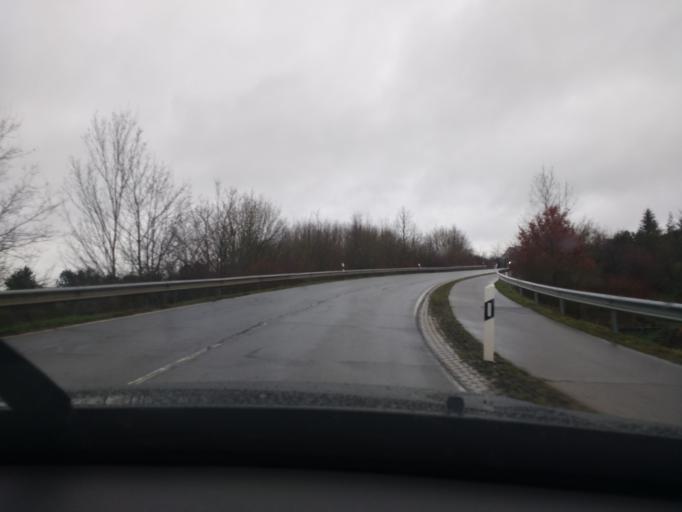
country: DE
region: Rheinland-Pfalz
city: Irsch
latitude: 49.7333
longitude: 6.7045
